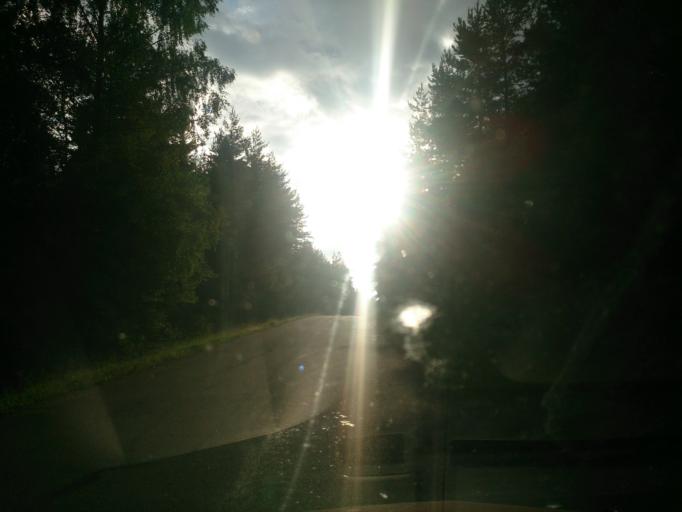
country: SE
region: OEstergoetland
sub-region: Norrkopings Kommun
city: Jursla
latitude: 58.7233
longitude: 16.1304
